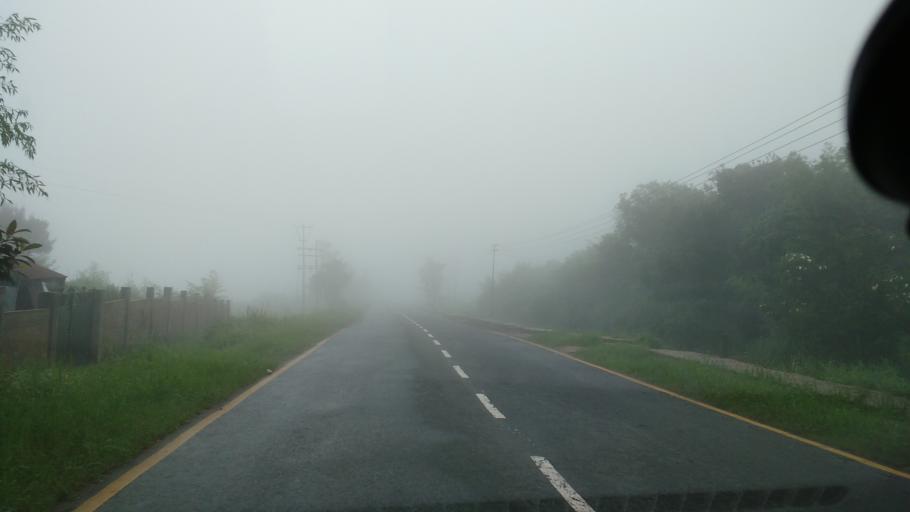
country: IN
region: Meghalaya
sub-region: East Khasi Hills
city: Cherrapunji
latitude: 25.3463
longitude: 91.7383
